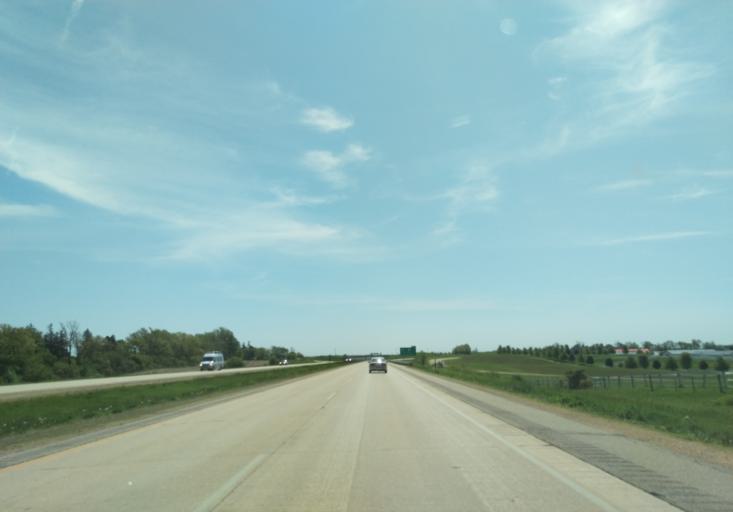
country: US
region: Wisconsin
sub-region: Dane County
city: Mount Horeb
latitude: 43.0047
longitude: -89.7687
